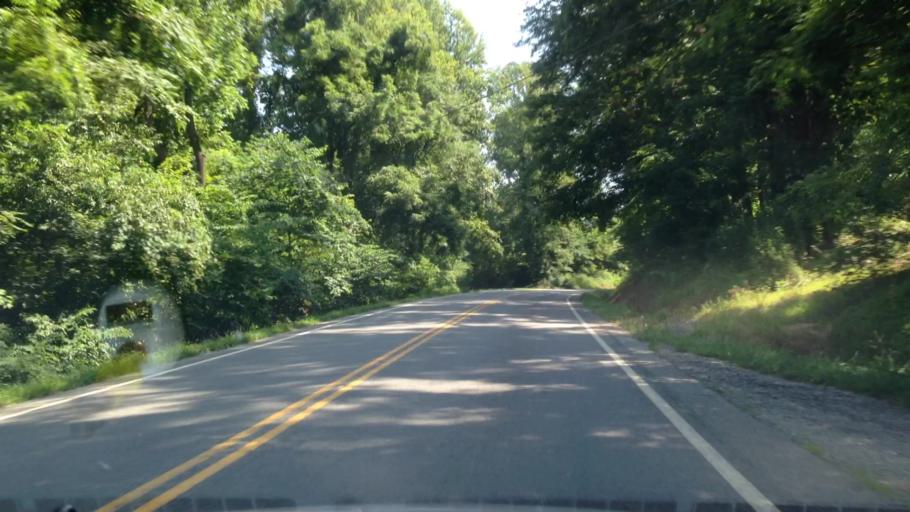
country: US
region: Virginia
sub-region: Patrick County
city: Stuart
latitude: 36.5882
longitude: -80.3302
